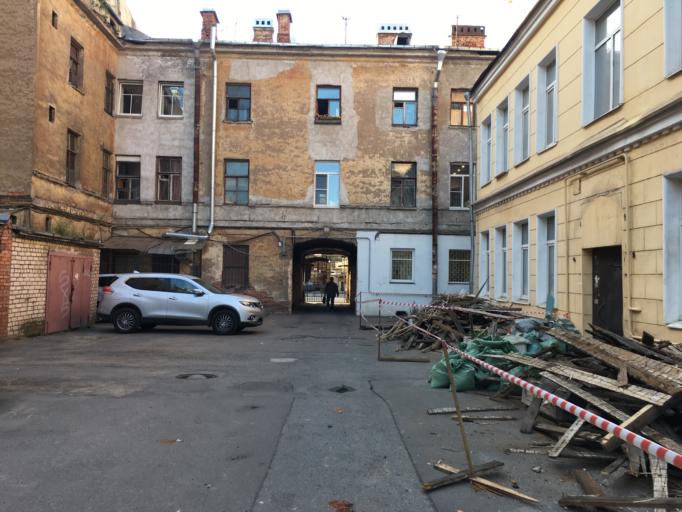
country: RU
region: St.-Petersburg
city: Centralniy
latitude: 59.9199
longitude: 30.3420
